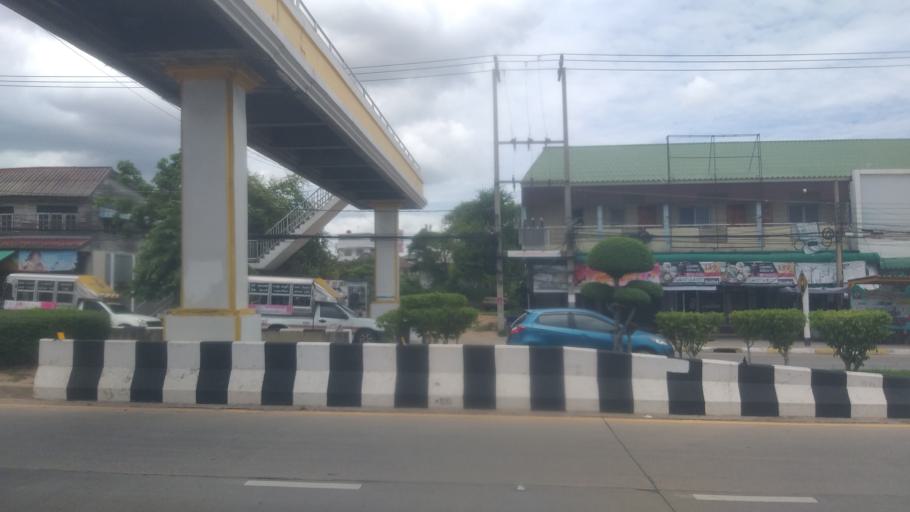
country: TH
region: Nakhon Ratchasima
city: Nakhon Ratchasima
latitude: 15.0292
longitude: 102.1380
